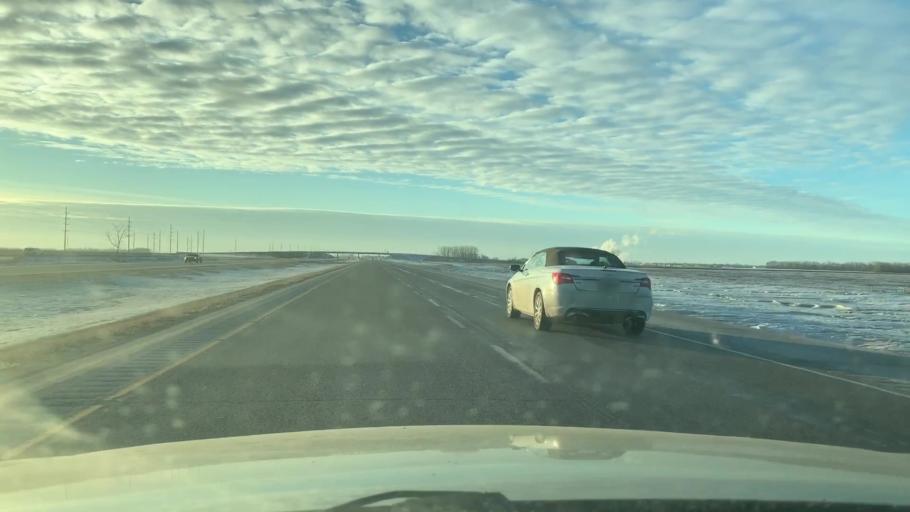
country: US
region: North Dakota
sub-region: Cass County
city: Casselton
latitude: 46.8768
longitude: -97.1484
